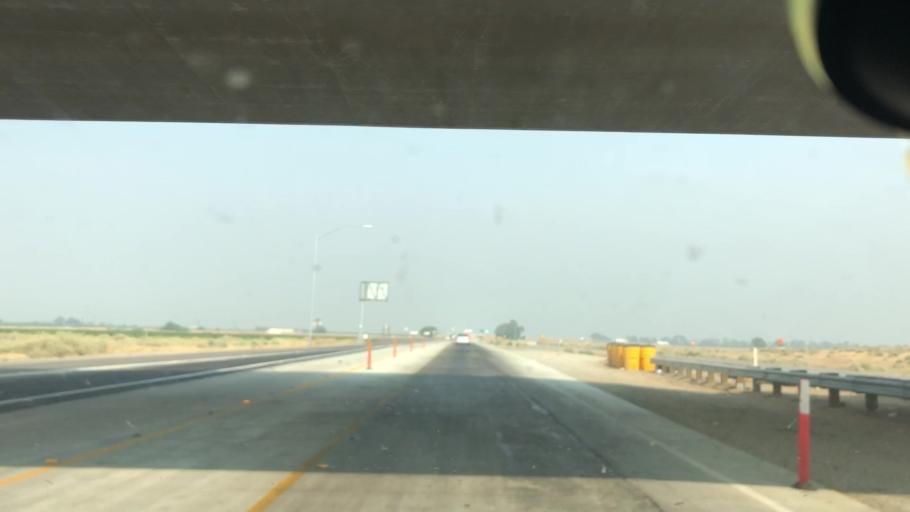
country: US
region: California
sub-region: San Joaquin County
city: Tracy
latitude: 37.6379
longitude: -121.3612
